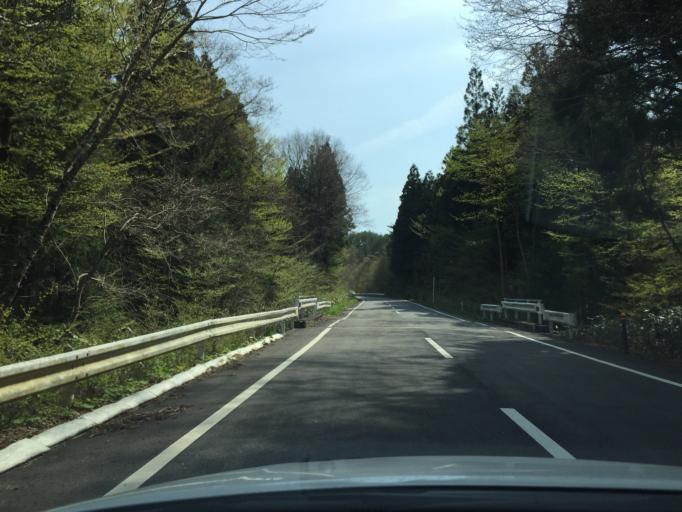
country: JP
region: Fukushima
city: Iwaki
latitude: 37.2485
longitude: 140.8482
